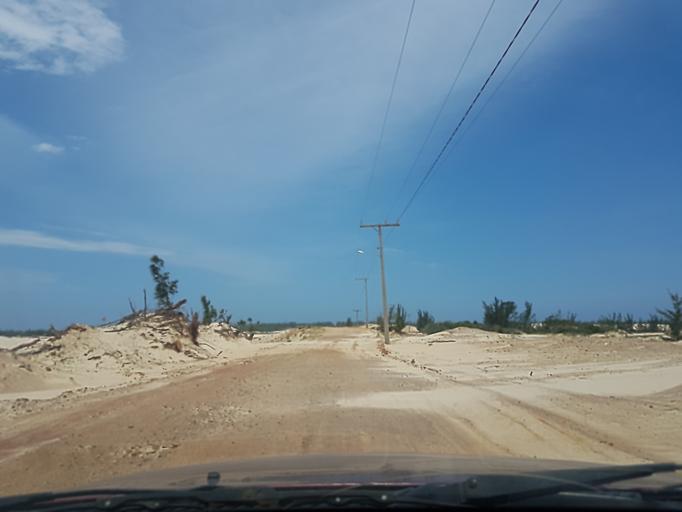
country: BR
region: Santa Catarina
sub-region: Jaguaruna
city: Jaguaruna
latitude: -28.6510
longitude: -48.9601
